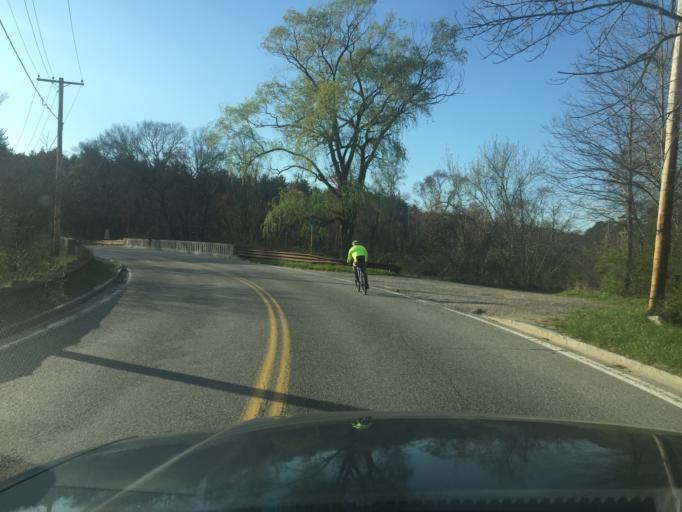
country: US
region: Massachusetts
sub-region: Middlesex County
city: Sherborn
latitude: 42.2324
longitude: -71.3297
